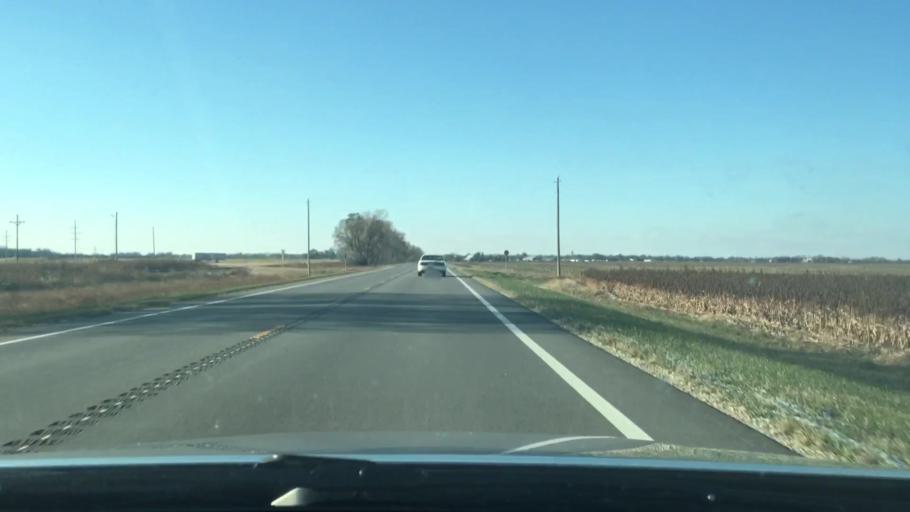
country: US
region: Kansas
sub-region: Reno County
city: Nickerson
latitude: 38.1295
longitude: -98.0576
